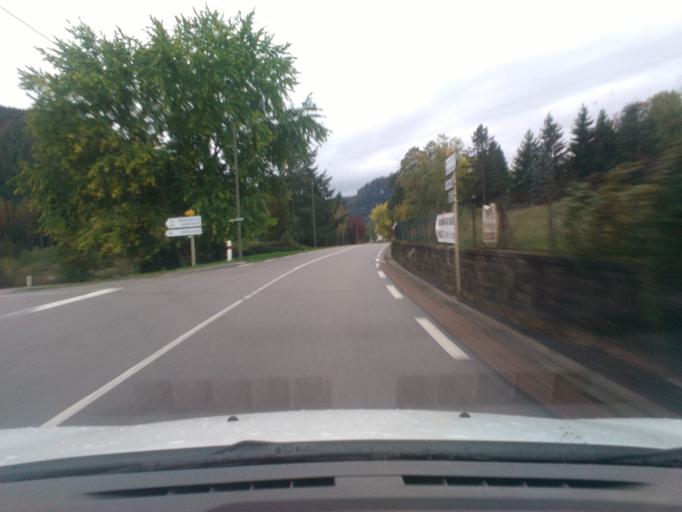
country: FR
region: Lorraine
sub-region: Departement des Vosges
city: Taintrux
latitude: 48.2744
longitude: 6.8995
